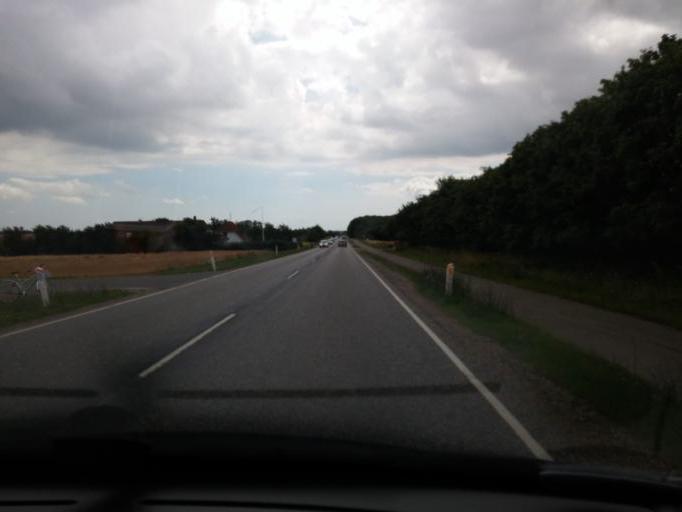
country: DK
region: South Denmark
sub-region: Svendborg Kommune
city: Vindeby
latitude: 55.0161
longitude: 10.6081
